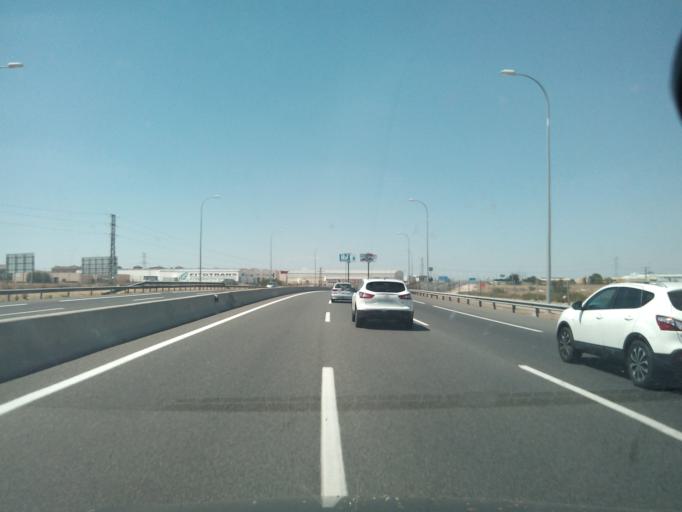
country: ES
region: Castille-La Mancha
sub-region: Province of Toledo
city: Sesena
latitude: 40.1207
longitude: -3.6549
